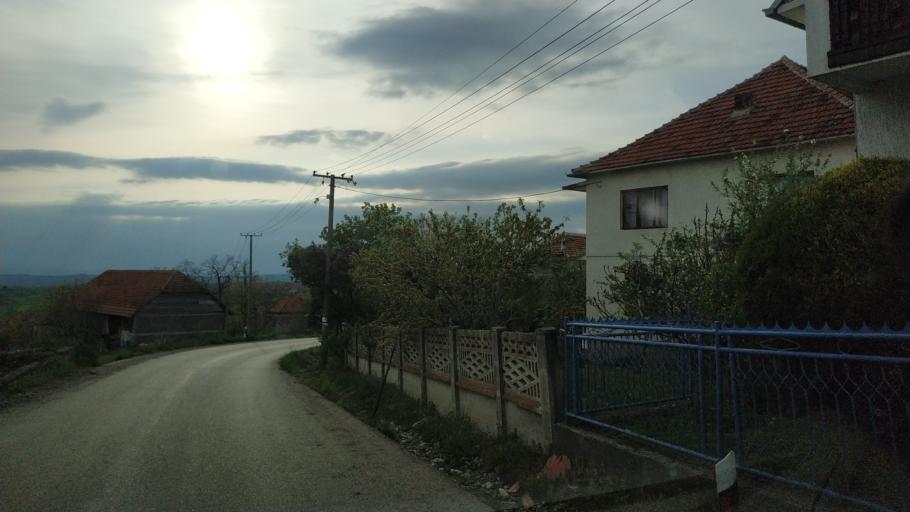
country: RS
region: Central Serbia
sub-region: Zajecarski Okrug
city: Soko Banja
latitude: 43.5238
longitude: 21.8631
